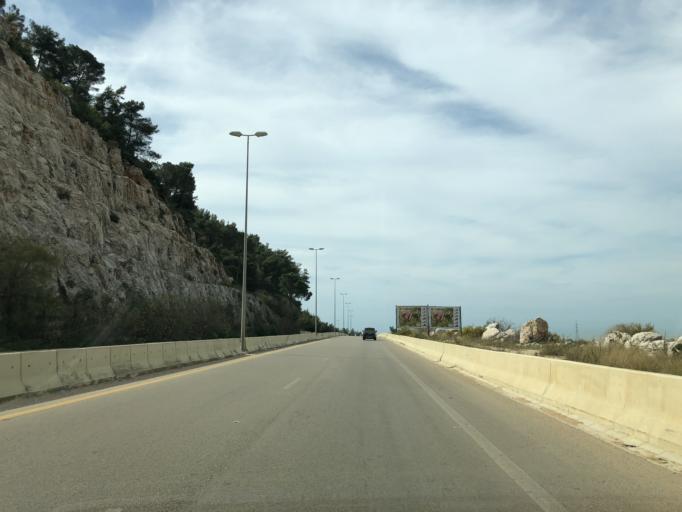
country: LB
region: Mont-Liban
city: Jdaidet el Matn
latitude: 33.8996
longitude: 35.6454
